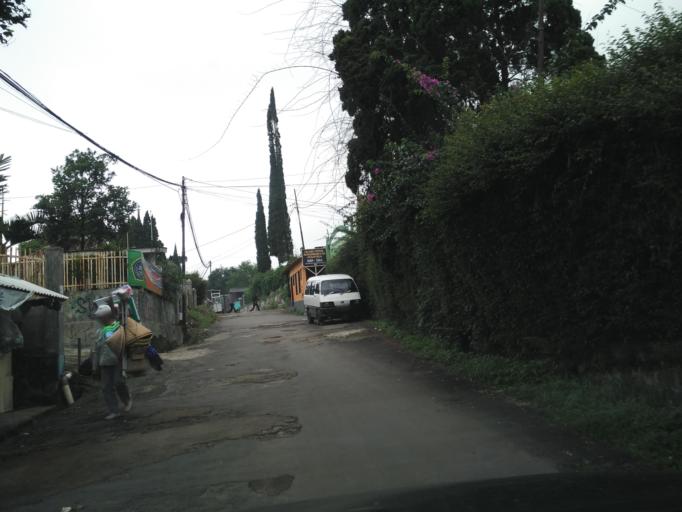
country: ID
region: West Java
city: Sukabumi
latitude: -6.7392
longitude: 107.0415
